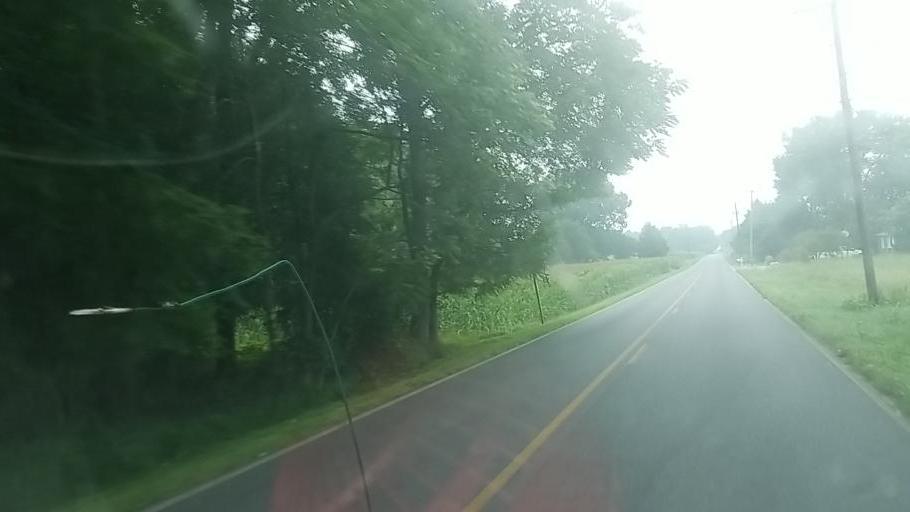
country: US
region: Maryland
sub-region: Wicomico County
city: Salisbury
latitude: 38.3891
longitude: -75.5296
